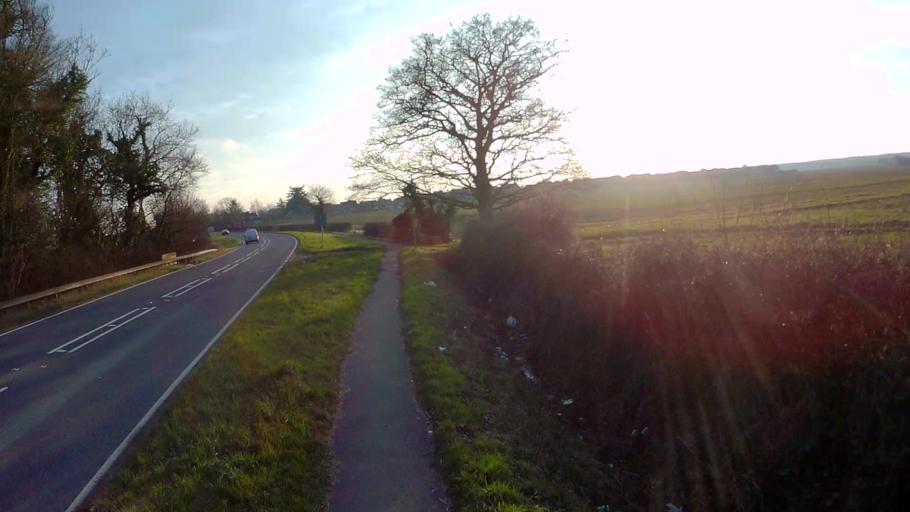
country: GB
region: England
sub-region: Lincolnshire
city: Bourne
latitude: 52.7817
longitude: -0.3769
